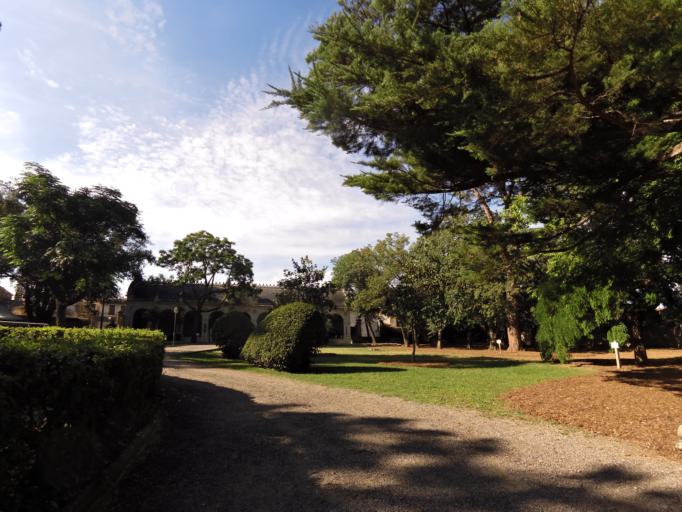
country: FR
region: Languedoc-Roussillon
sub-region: Departement de l'Herault
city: Lunel-Viel
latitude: 43.6790
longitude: 4.0932
